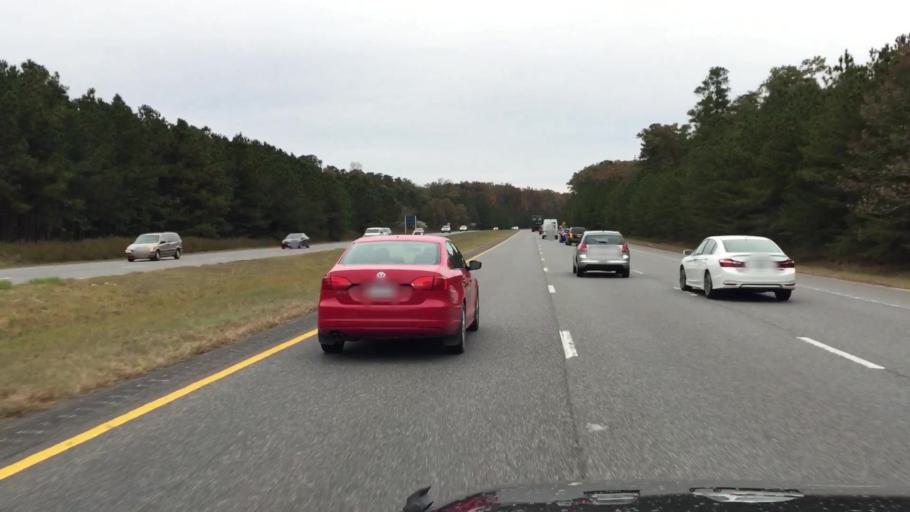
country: US
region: Virginia
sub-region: James City County
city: Williamsburg
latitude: 37.2769
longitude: -76.7528
